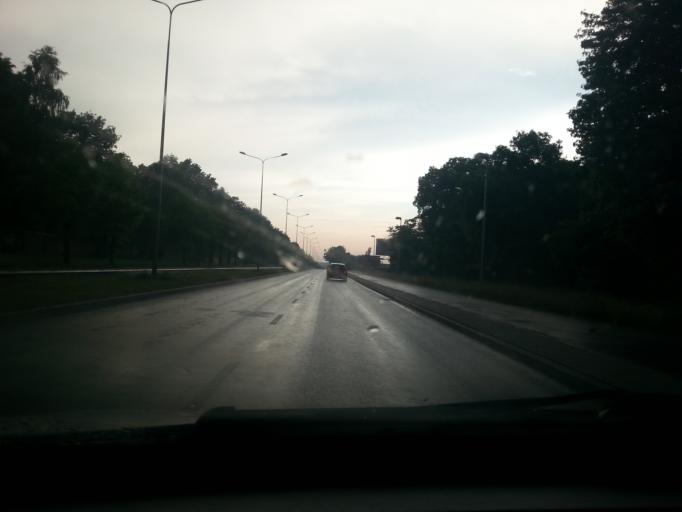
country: PL
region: Lodz Voivodeship
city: Lodz
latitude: 51.7999
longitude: 19.4853
